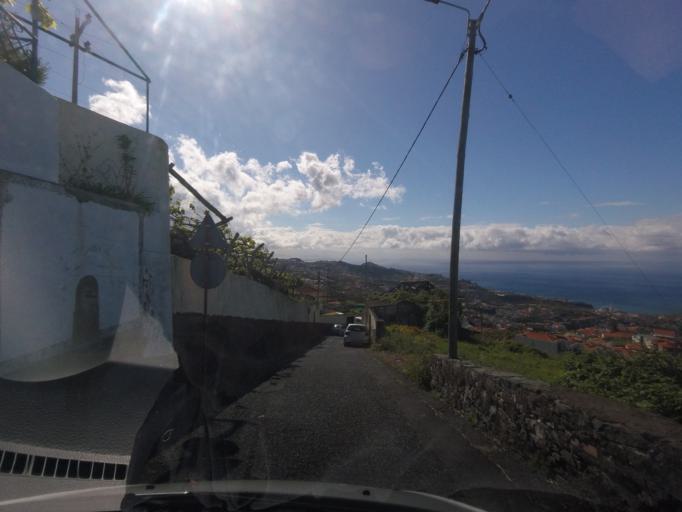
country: PT
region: Madeira
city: Camara de Lobos
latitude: 32.6667
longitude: -16.9759
